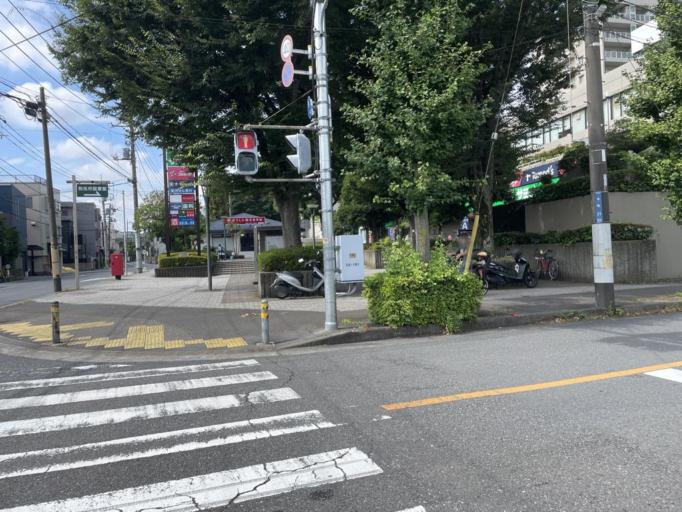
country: JP
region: Saitama
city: Wako
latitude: 35.7875
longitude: 139.6083
